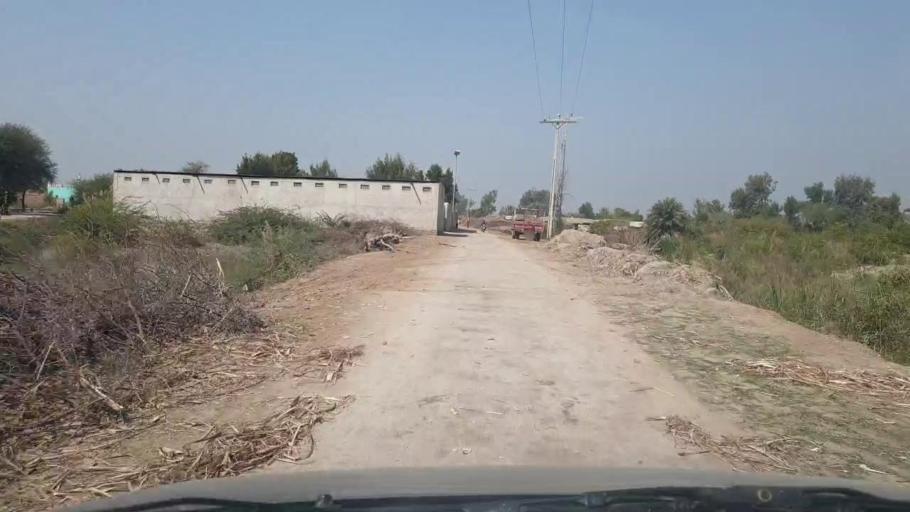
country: PK
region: Sindh
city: Mirwah Gorchani
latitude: 25.3546
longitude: 69.1469
